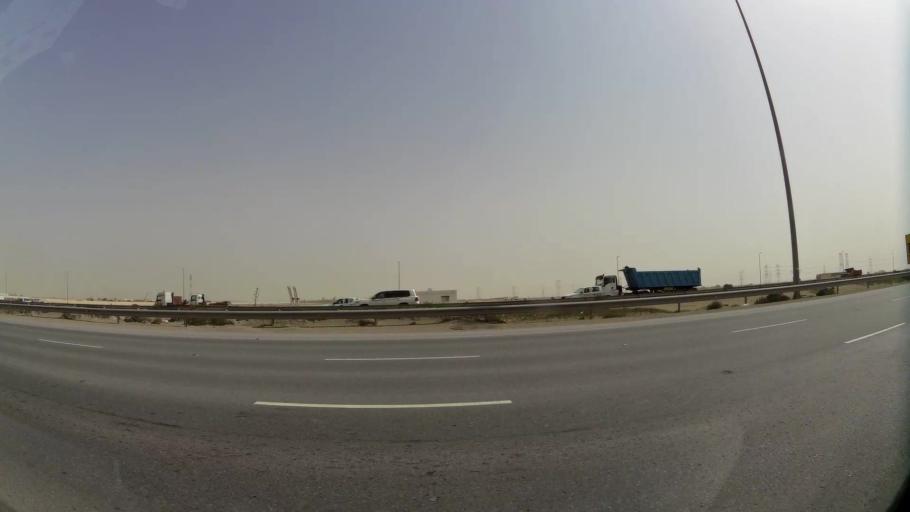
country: QA
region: Baladiyat ar Rayyan
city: Ar Rayyan
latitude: 25.1781
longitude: 51.3414
